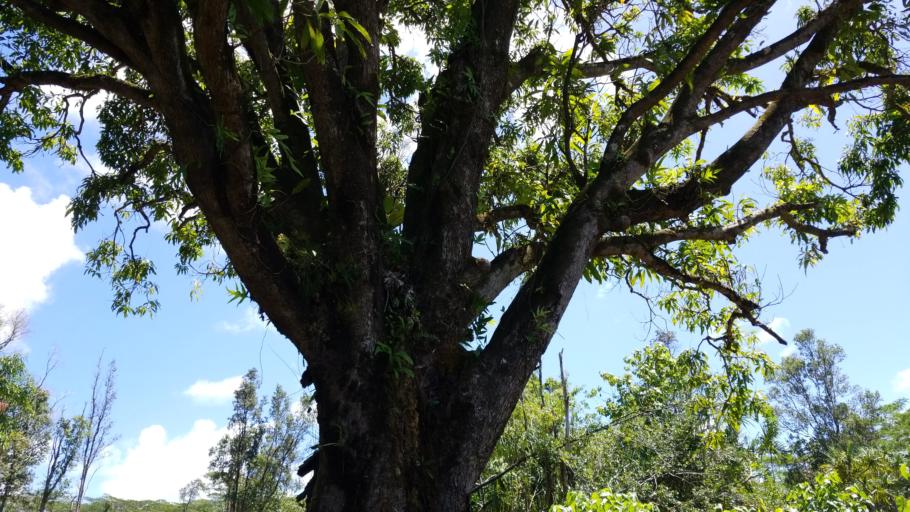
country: US
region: Hawaii
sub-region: Hawaii County
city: Hawaiian Beaches
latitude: 19.5430
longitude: -154.8687
